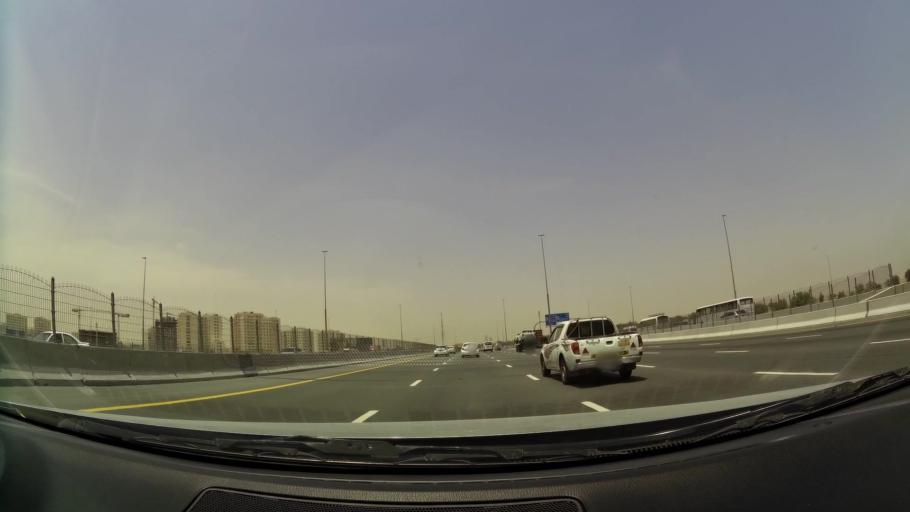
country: AE
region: Dubai
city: Dubai
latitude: 25.1203
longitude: 55.3649
